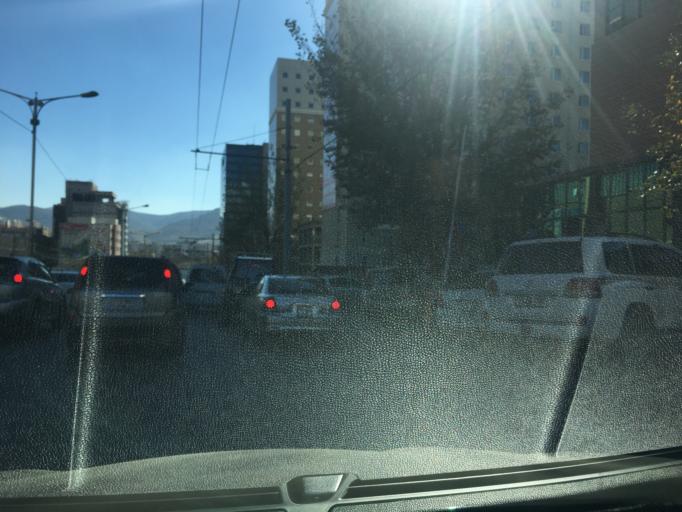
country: MN
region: Ulaanbaatar
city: Ulaanbaatar
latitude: 47.9166
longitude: 106.8909
